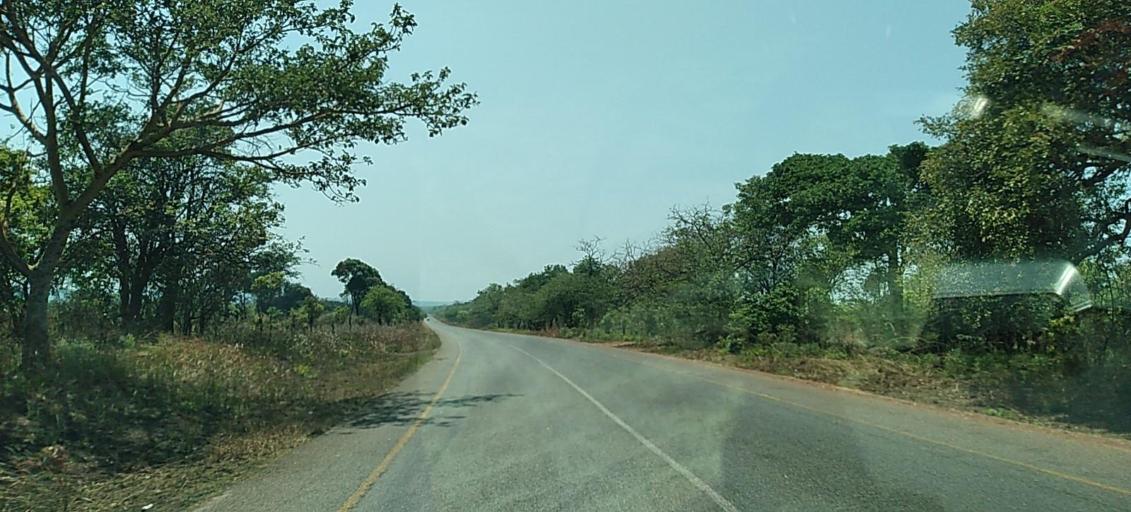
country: ZM
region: North-Western
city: Solwezi
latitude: -12.3925
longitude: 26.2121
